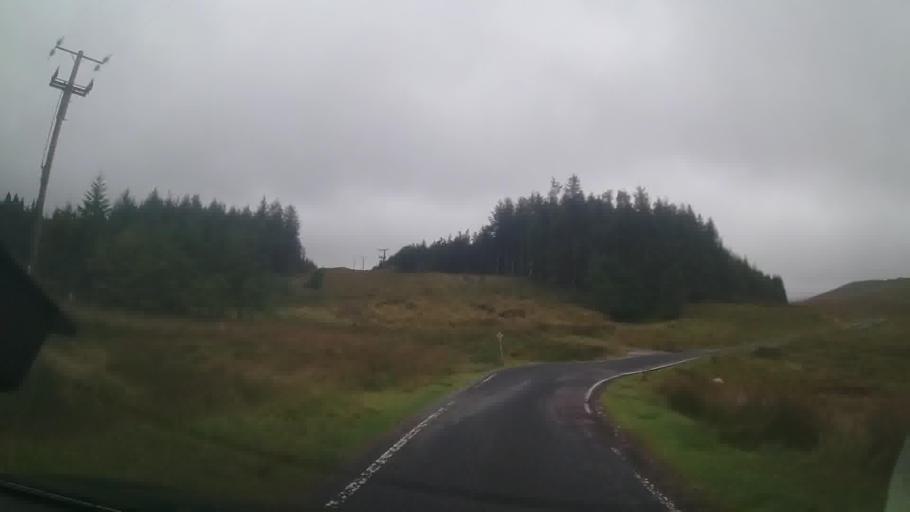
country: GB
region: Scotland
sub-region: Argyll and Bute
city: Isle Of Mull
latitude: 56.7251
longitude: -6.0391
